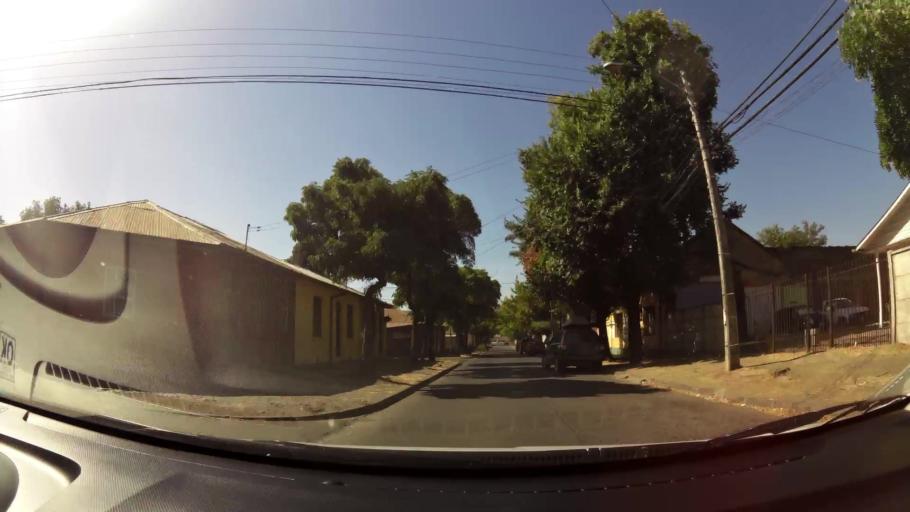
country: CL
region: Maule
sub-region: Provincia de Talca
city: Talca
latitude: -35.4177
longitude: -71.6630
